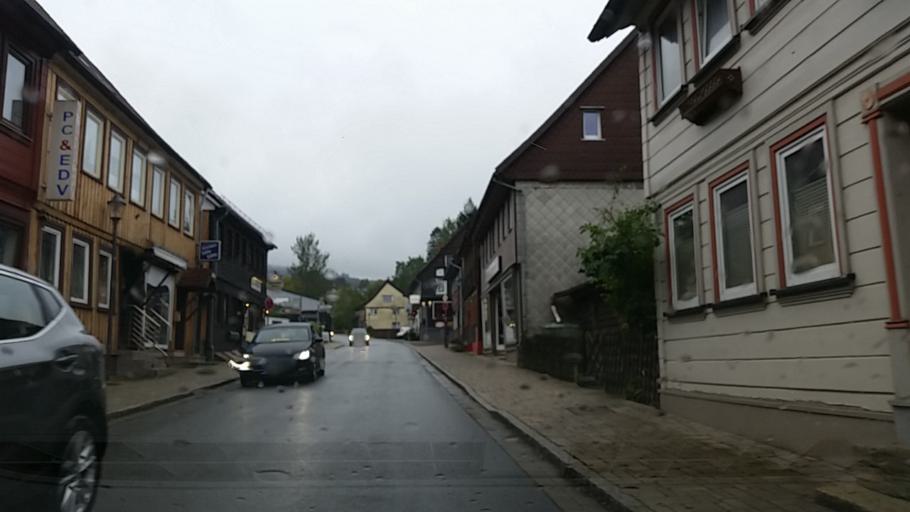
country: DE
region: Lower Saxony
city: Altenau
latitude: 51.8015
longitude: 10.4479
